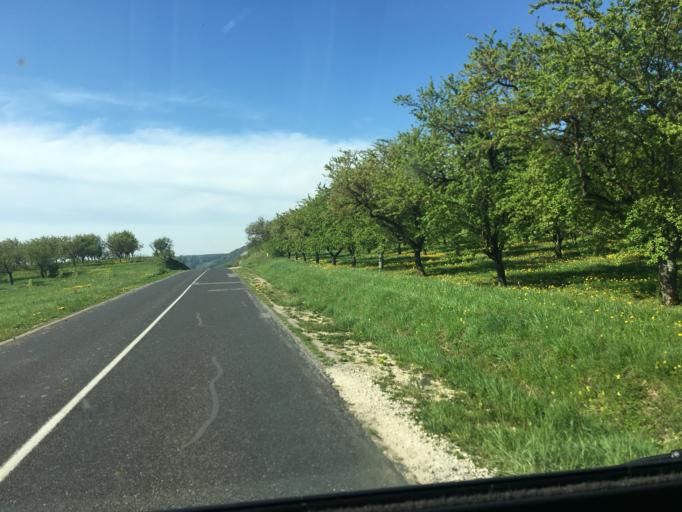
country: FR
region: Lorraine
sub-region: Departement de la Meuse
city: Vigneulles-les-Hattonchatel
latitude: 48.9209
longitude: 5.6818
